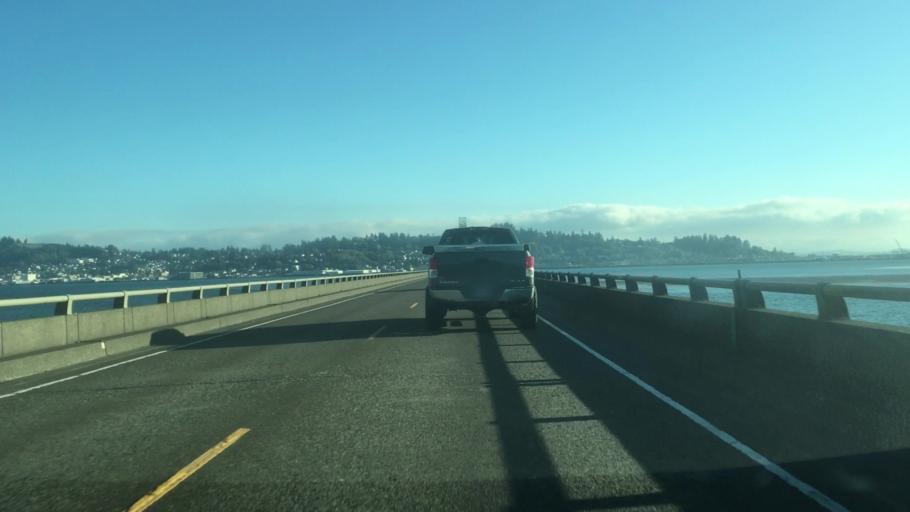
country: US
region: Oregon
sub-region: Clatsop County
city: Astoria
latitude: 46.2102
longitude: -123.8594
